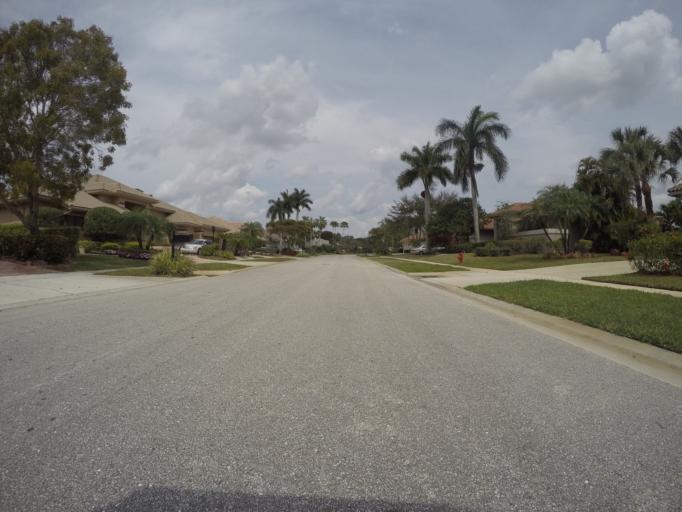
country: US
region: Florida
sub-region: Palm Beach County
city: Villages of Oriole
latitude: 26.4137
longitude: -80.2213
